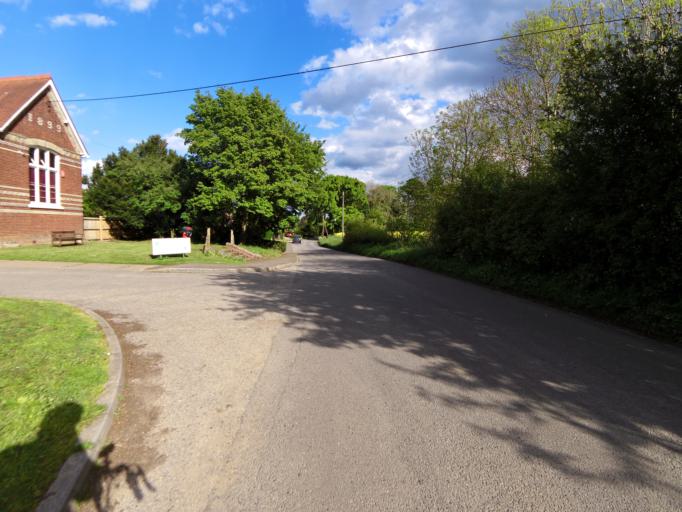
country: GB
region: England
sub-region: Suffolk
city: Stowmarket
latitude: 52.1980
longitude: 0.9546
